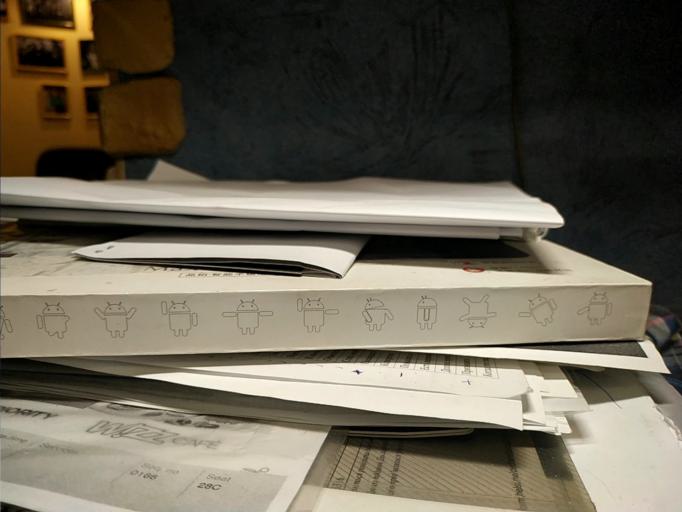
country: RU
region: Tverskaya
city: Zubtsov
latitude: 56.0843
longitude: 34.7787
